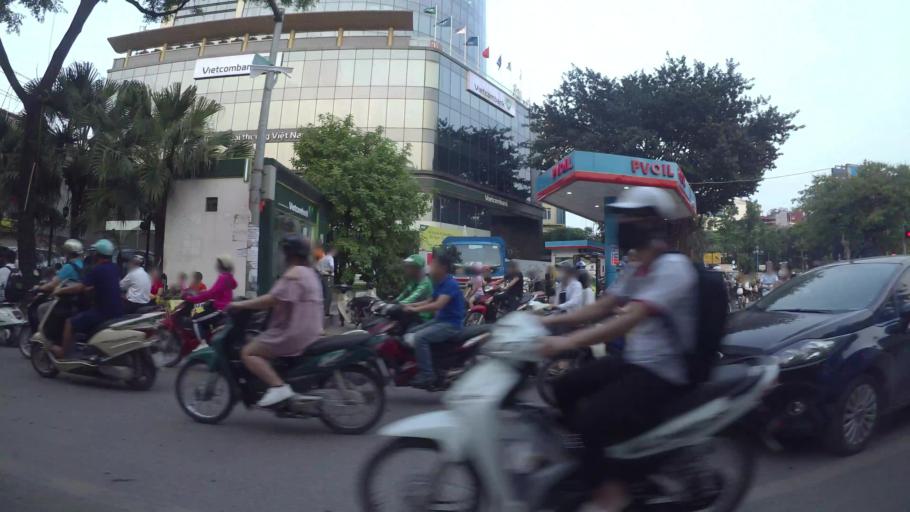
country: VN
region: Ha Noi
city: Cau Giay
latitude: 21.0466
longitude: 105.7904
